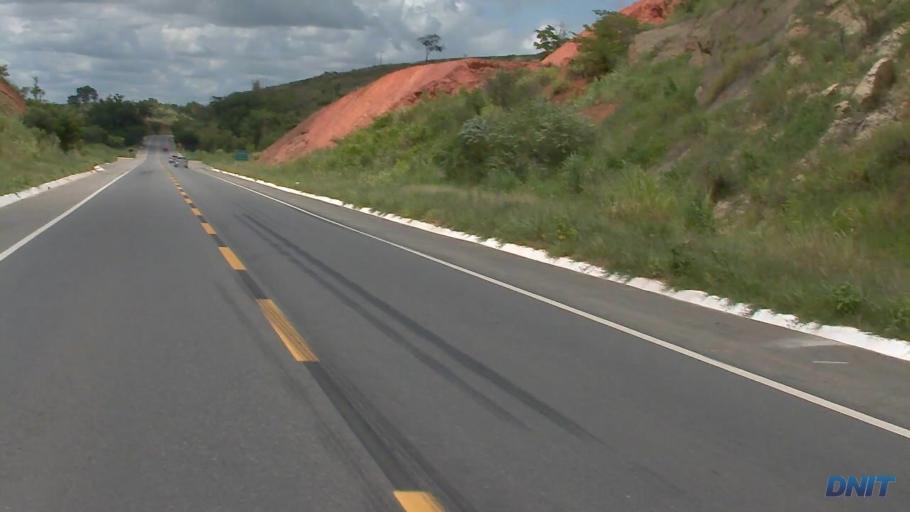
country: BR
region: Minas Gerais
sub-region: Governador Valadares
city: Governador Valadares
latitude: -18.9206
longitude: -42.0155
